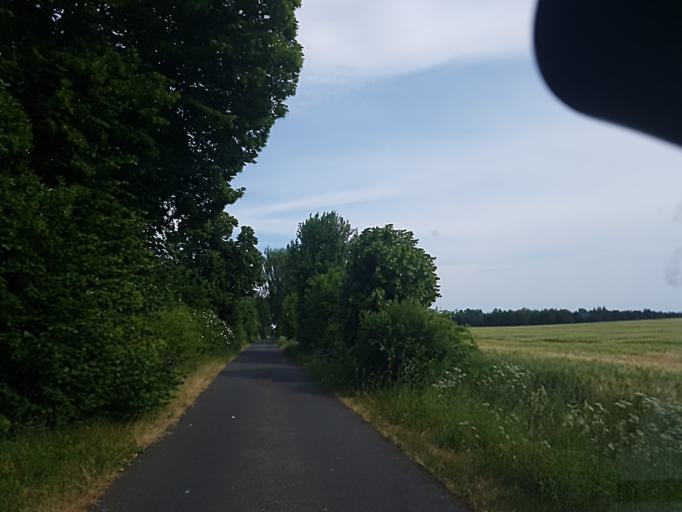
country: DE
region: Brandenburg
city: Niemegk
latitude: 52.0078
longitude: 12.6636
